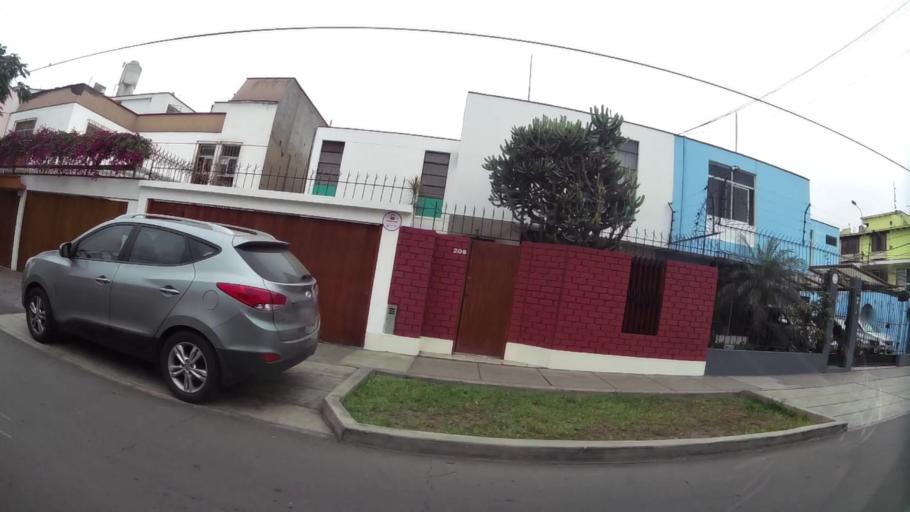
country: PE
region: Lima
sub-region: Lima
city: Surco
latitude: -12.1295
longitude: -76.9922
